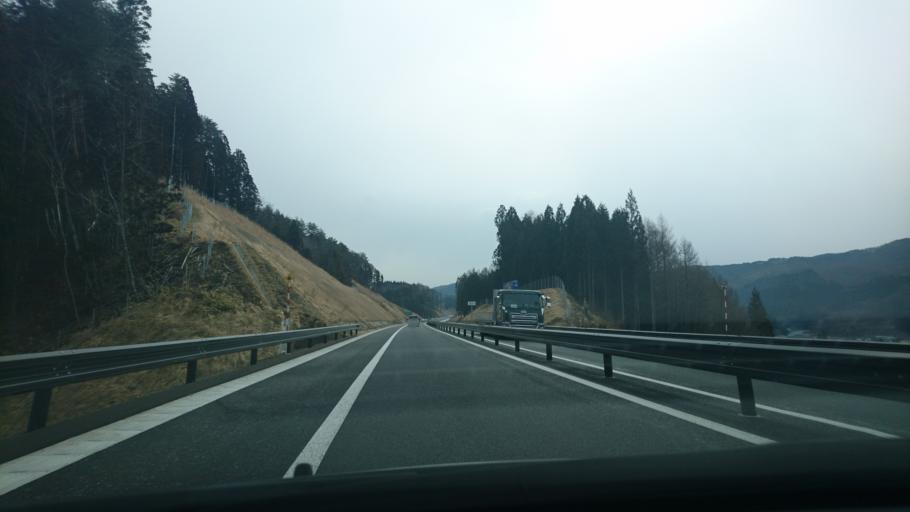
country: JP
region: Iwate
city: Tono
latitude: 39.2847
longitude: 141.5508
